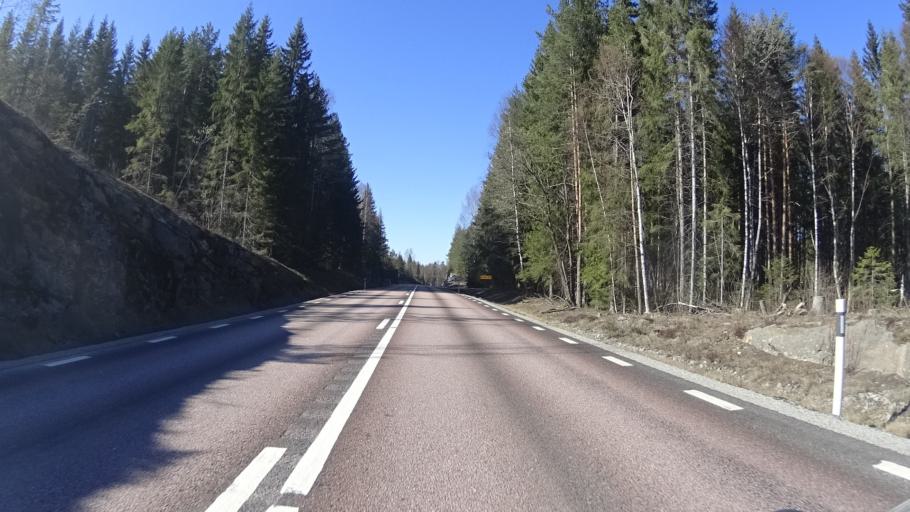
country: SE
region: Vaermland
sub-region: Karlstads Kommun
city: Edsvalla
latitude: 59.6052
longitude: 12.9950
